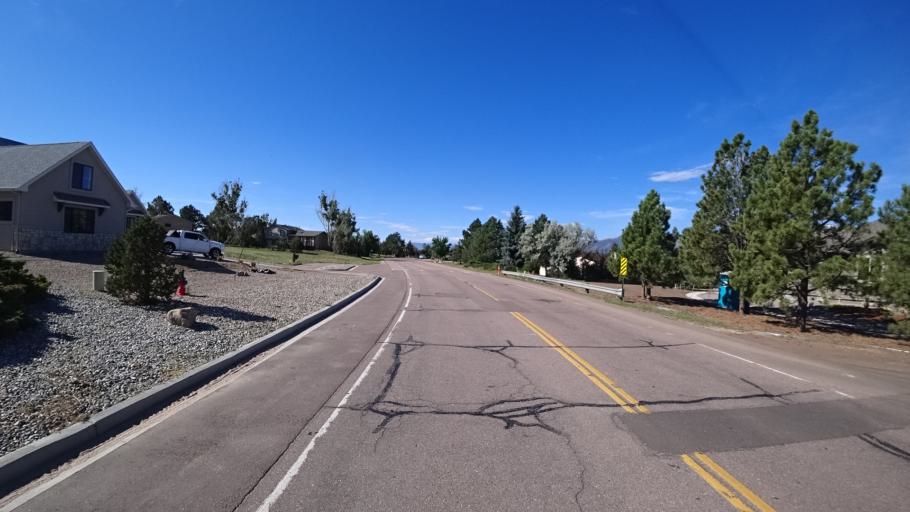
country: US
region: Colorado
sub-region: El Paso County
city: Gleneagle
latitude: 39.0350
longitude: -104.8281
